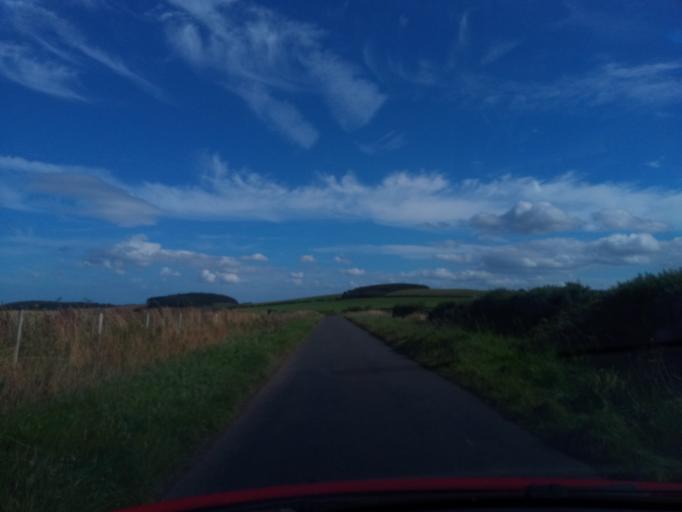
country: GB
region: England
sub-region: Northumberland
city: Kirknewton
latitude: 55.6166
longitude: -2.1735
